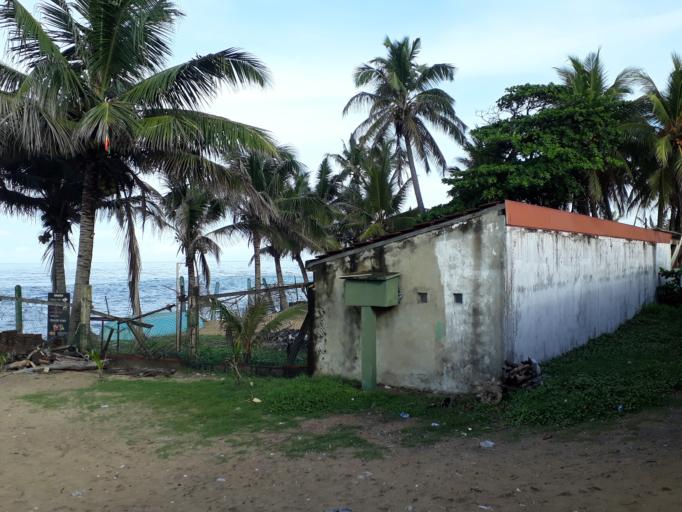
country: LK
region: Western
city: Pita Kotte
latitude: 6.8763
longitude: 79.8571
